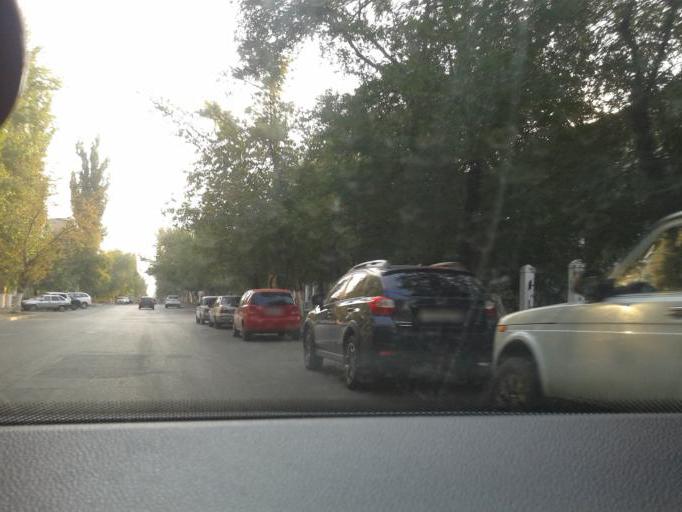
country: RU
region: Volgograd
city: Volgograd
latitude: 48.7010
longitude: 44.5003
